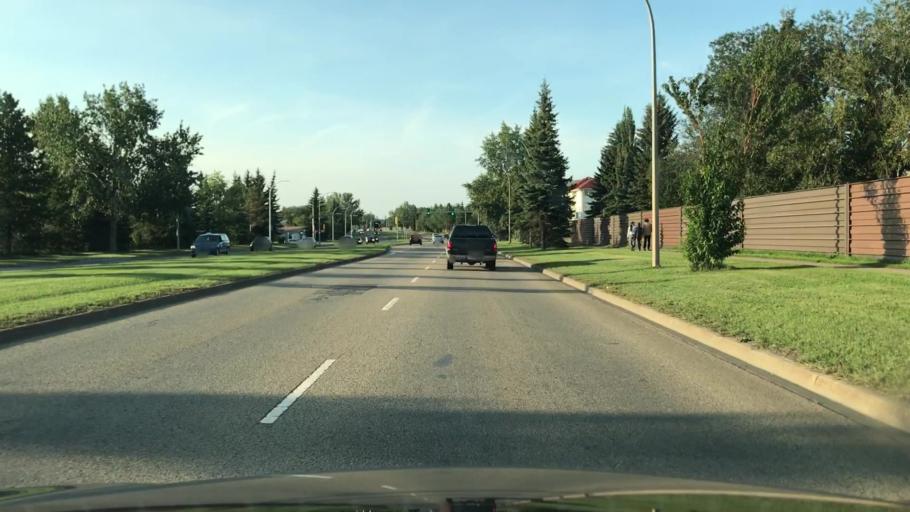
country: CA
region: Alberta
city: Beaumont
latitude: 53.4482
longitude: -113.4193
